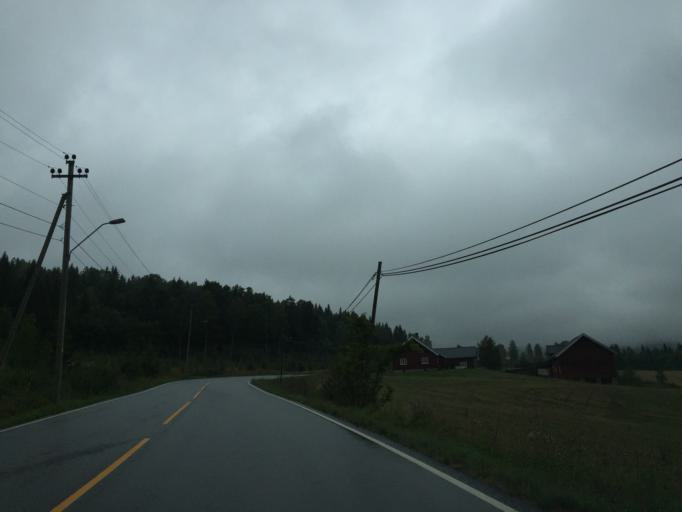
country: NO
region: Akershus
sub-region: Baerum
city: Lysaker
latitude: 60.0014
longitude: 10.6192
